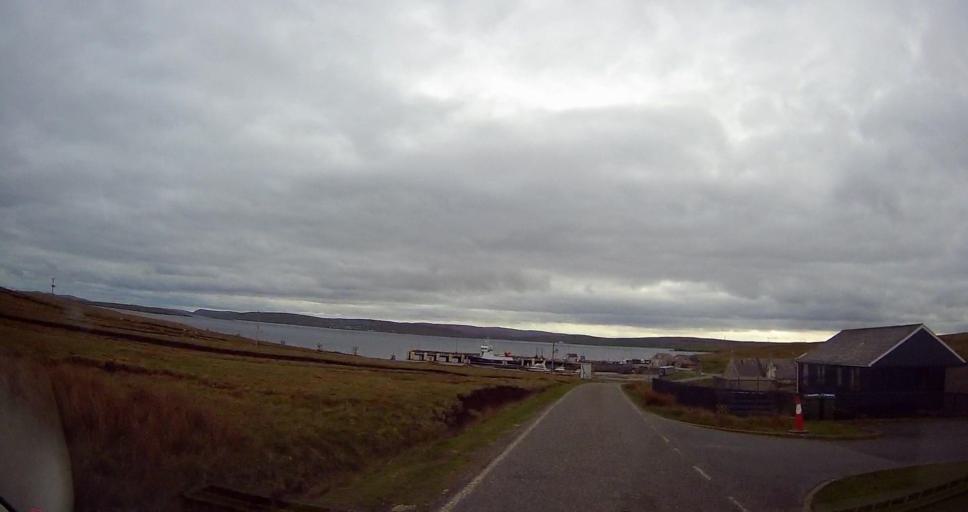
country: GB
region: Scotland
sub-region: Shetland Islands
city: Shetland
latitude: 60.4991
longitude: -1.1544
